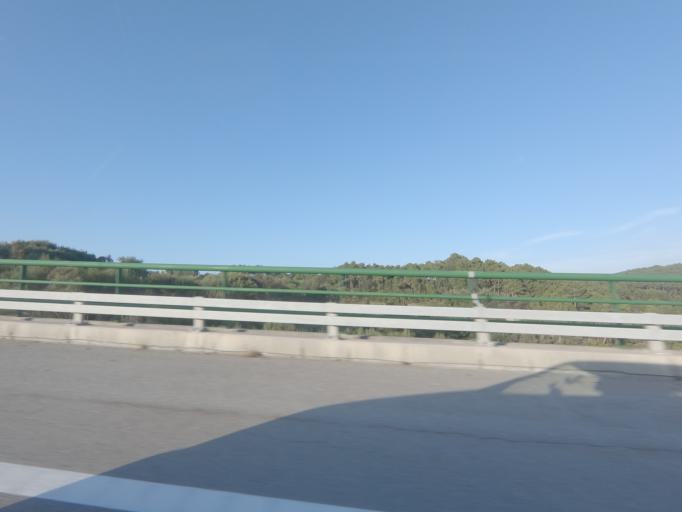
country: PT
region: Vila Real
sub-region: Vila Real
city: Vila Real
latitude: 41.3110
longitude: -7.6865
